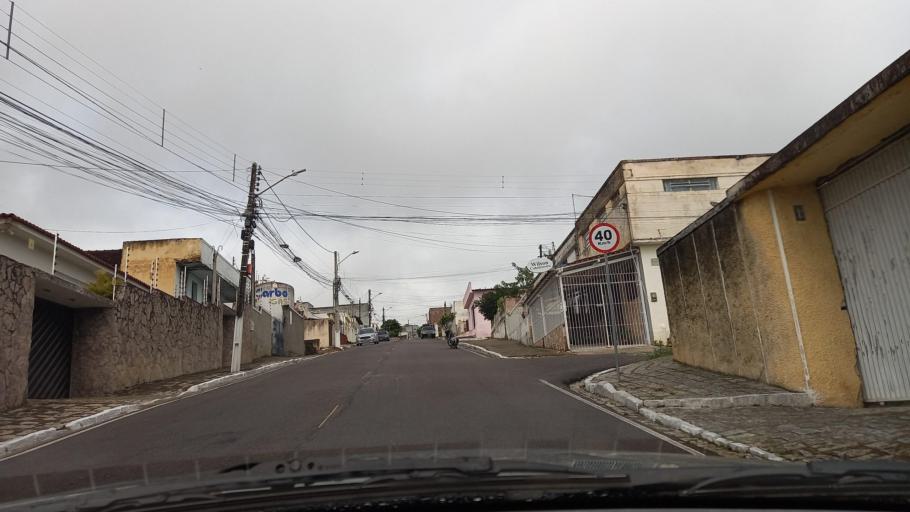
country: BR
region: Pernambuco
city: Garanhuns
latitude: -8.8946
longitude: -36.4919
